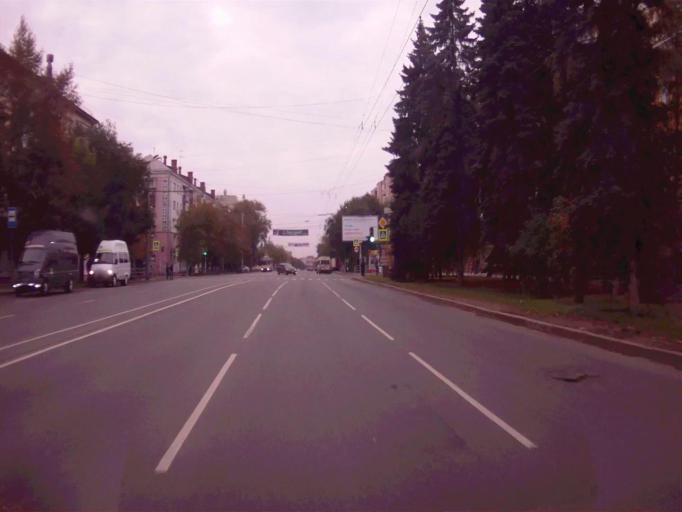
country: RU
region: Chelyabinsk
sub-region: Gorod Chelyabinsk
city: Chelyabinsk
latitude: 55.1564
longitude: 61.4134
